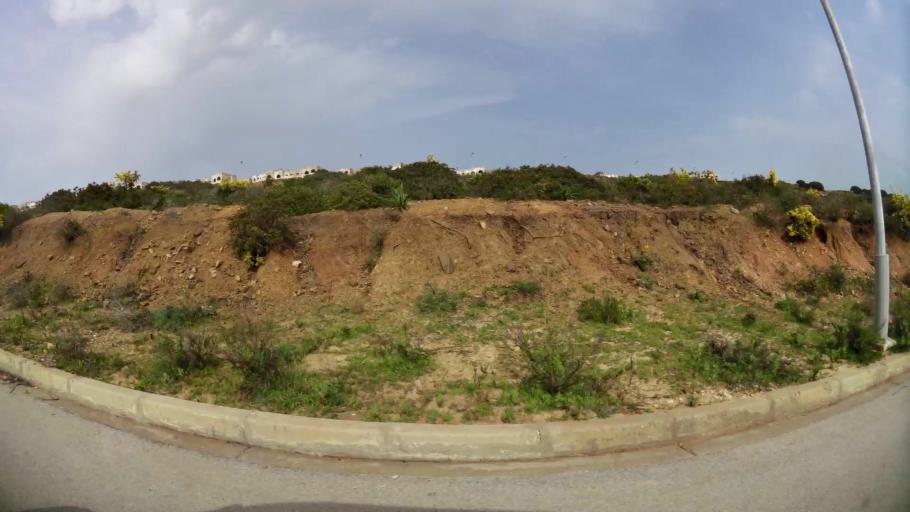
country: MA
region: Tanger-Tetouan
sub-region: Tanger-Assilah
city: Boukhalef
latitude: 35.6940
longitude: -5.9403
